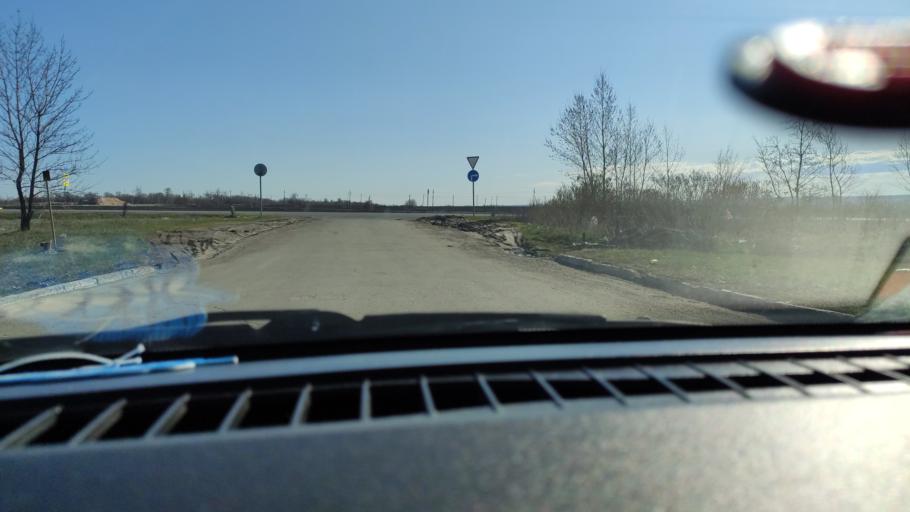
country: RU
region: Samara
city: Syzran'
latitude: 53.2051
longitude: 48.5094
